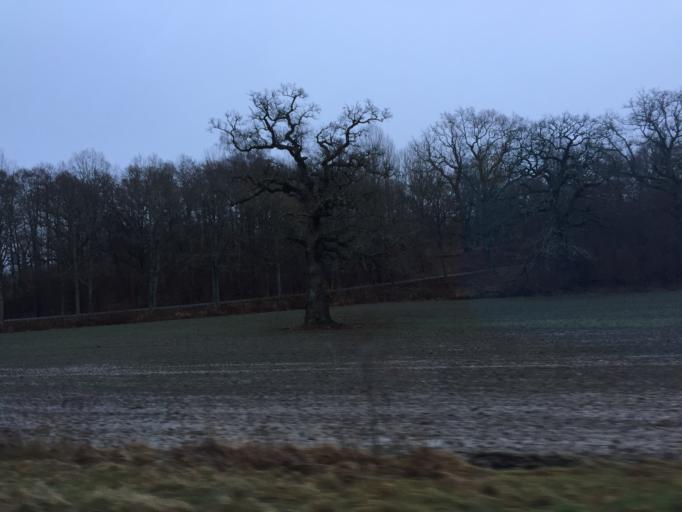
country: SE
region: Stockholm
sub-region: Nynashamns Kommun
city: Osmo
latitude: 59.0503
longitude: 18.0146
